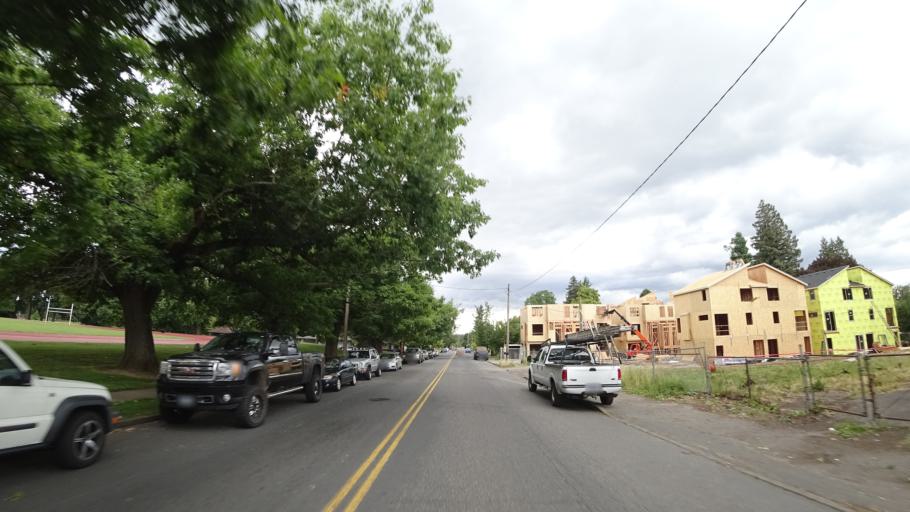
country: US
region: Oregon
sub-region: Multnomah County
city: Portland
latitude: 45.5654
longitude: -122.6204
